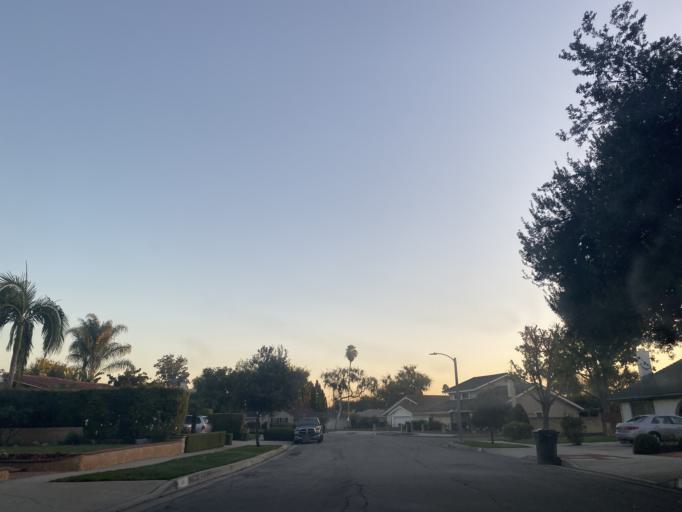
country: US
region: California
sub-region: Orange County
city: Fullerton
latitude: 33.8780
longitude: -117.9035
